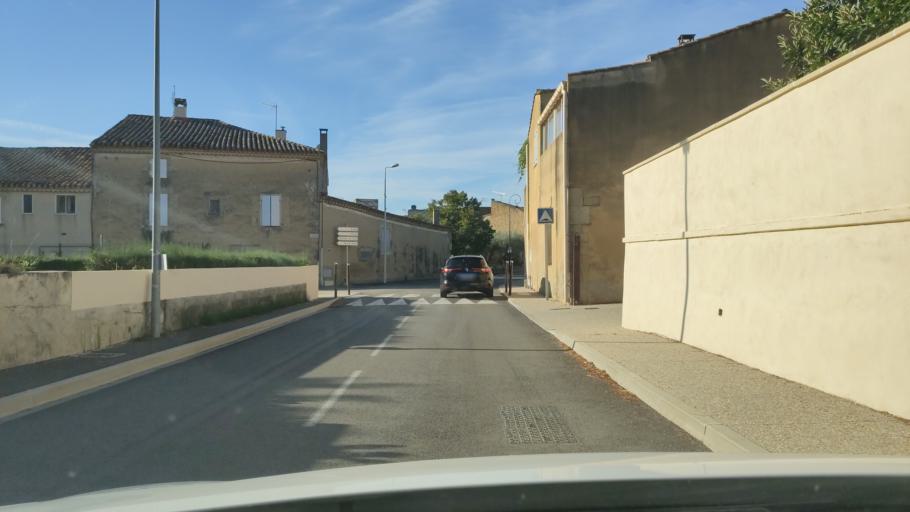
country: FR
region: Languedoc-Roussillon
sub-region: Departement du Gard
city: Saze
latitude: 43.9309
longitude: 4.6508
